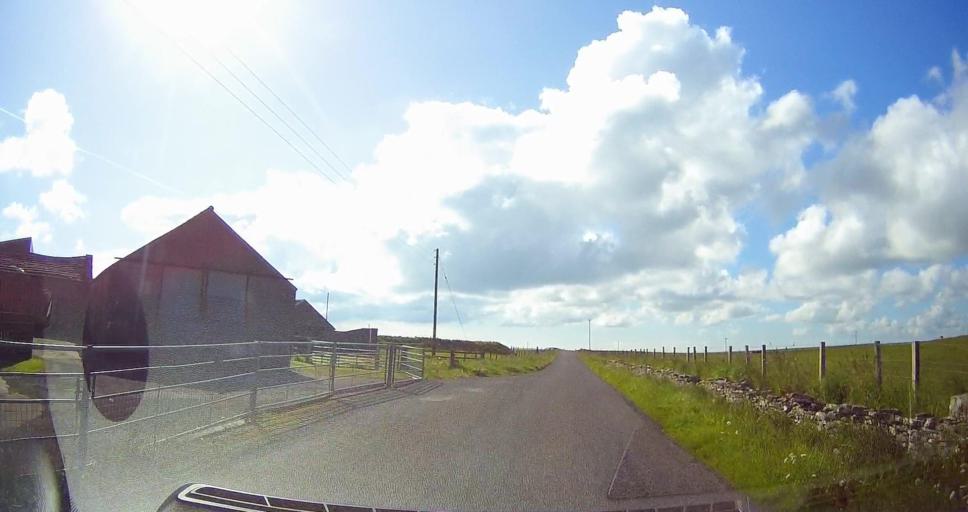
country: GB
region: Scotland
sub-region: Orkney Islands
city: Stromness
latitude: 58.9875
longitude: -3.1492
